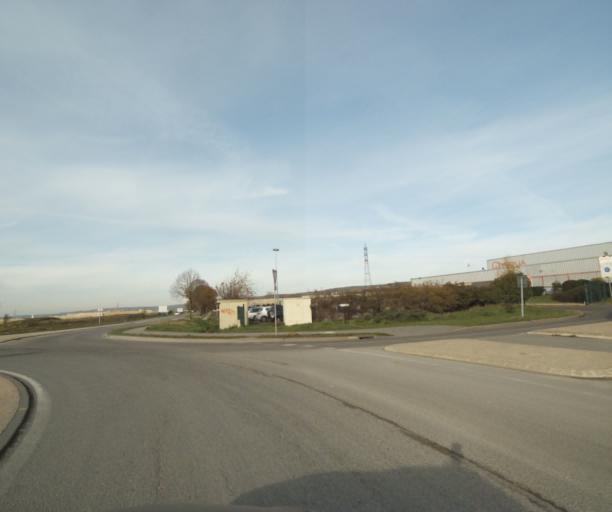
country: FR
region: Ile-de-France
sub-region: Departement des Yvelines
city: Carrieres-sous-Poissy
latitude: 48.9547
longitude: 2.0208
